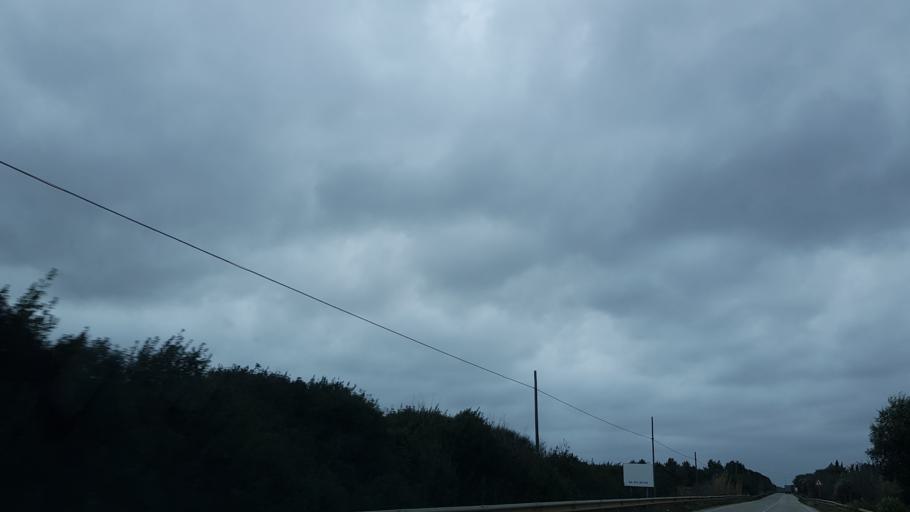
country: IT
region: Apulia
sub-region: Provincia di Brindisi
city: San Vito dei Normanni
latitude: 40.6532
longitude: 17.7874
